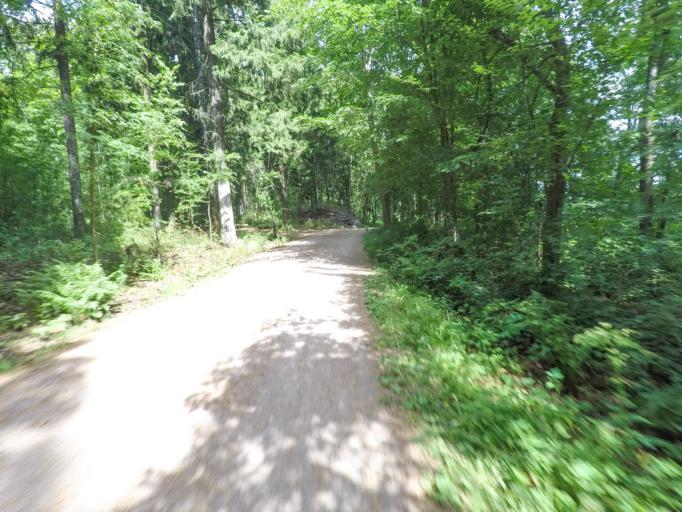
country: FI
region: Uusimaa
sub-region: Helsinki
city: Vantaa
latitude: 60.2189
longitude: 25.0082
